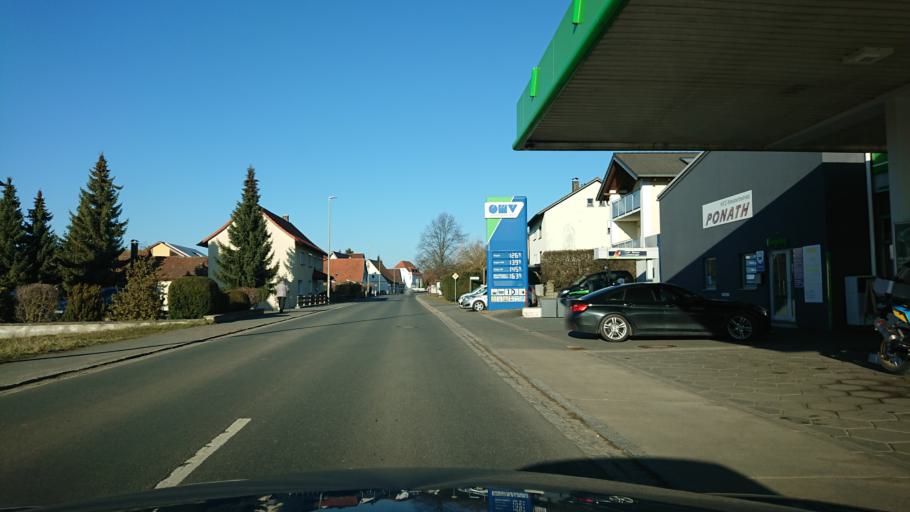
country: DE
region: Bavaria
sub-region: Upper Franconia
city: Kirchehrenbach
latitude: 49.7314
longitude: 11.1411
